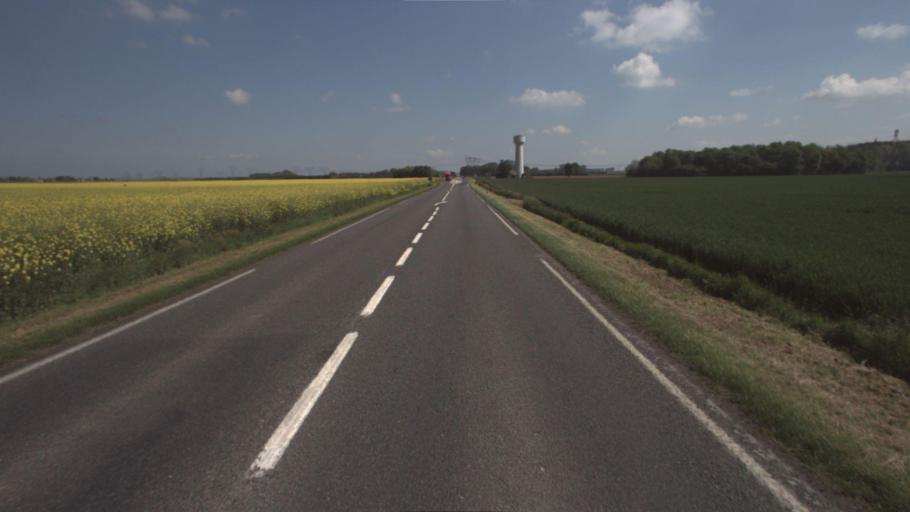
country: FR
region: Ile-de-France
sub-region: Departement de Seine-et-Marne
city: Moisenay
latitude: 48.6023
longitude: 2.7363
